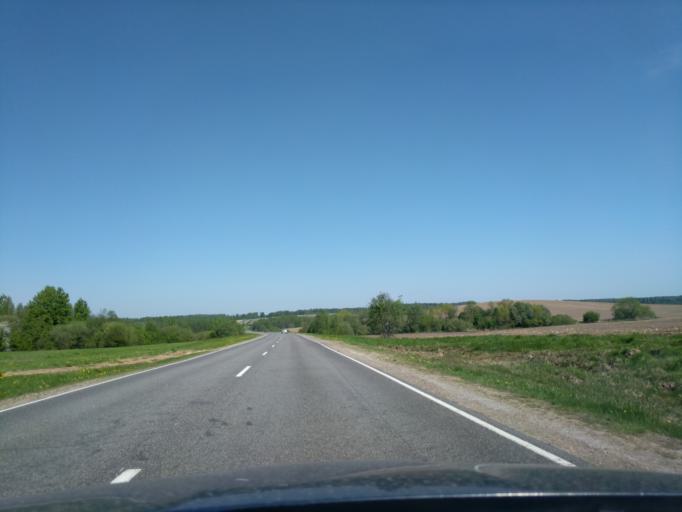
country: BY
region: Minsk
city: Il'ya
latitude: 54.2923
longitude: 27.4841
